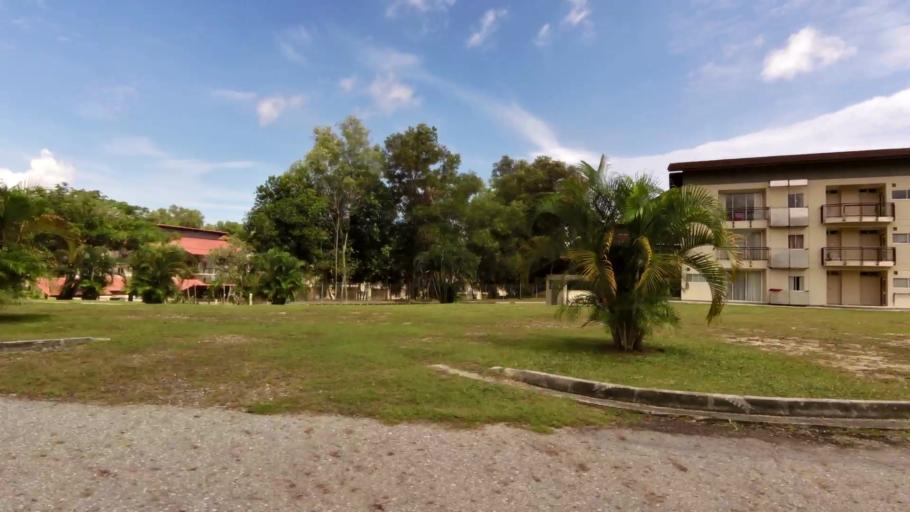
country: BN
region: Brunei and Muara
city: Bandar Seri Begawan
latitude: 4.9348
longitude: 114.8913
